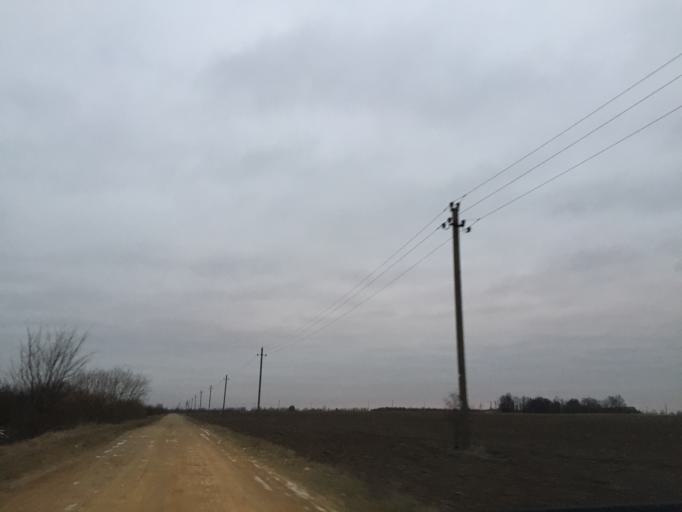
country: LT
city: Zagare
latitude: 56.3410
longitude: 23.2688
